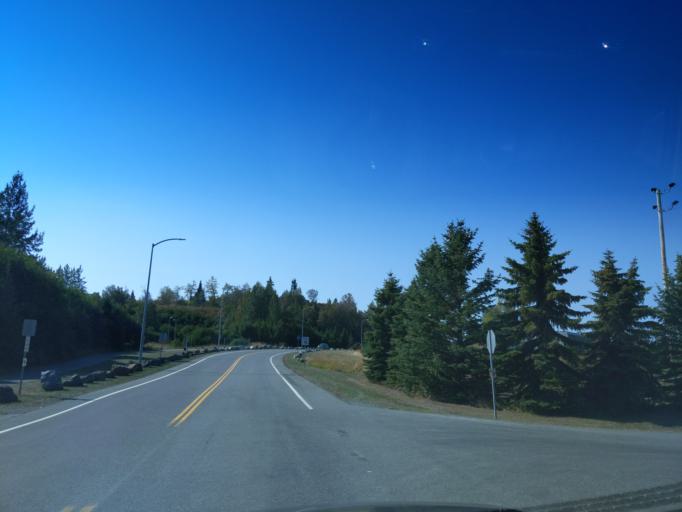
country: US
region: Alaska
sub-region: Anchorage Municipality
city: Anchorage
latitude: 61.1540
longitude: -150.0501
